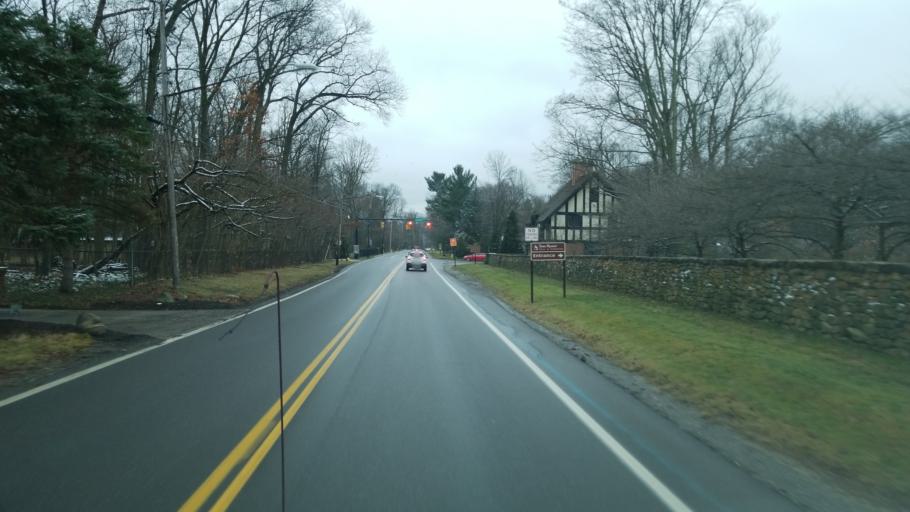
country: US
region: Ohio
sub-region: Summit County
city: Akron
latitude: 41.1174
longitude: -81.5486
